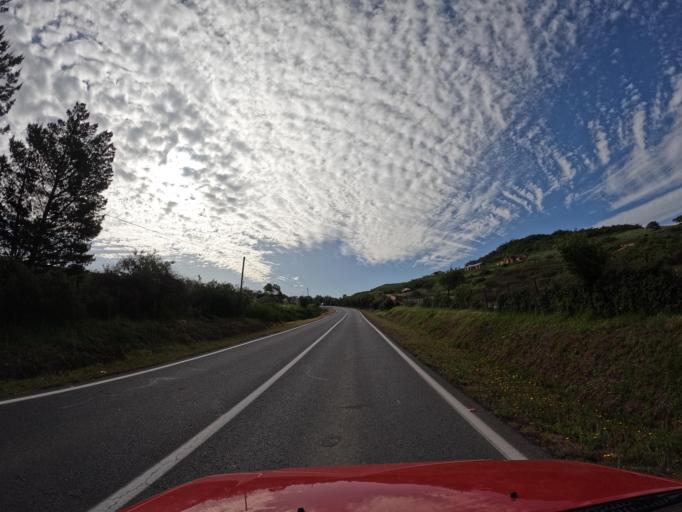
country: CL
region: O'Higgins
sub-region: Provincia de Colchagua
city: Santa Cruz
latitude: -34.2109
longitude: -71.7274
